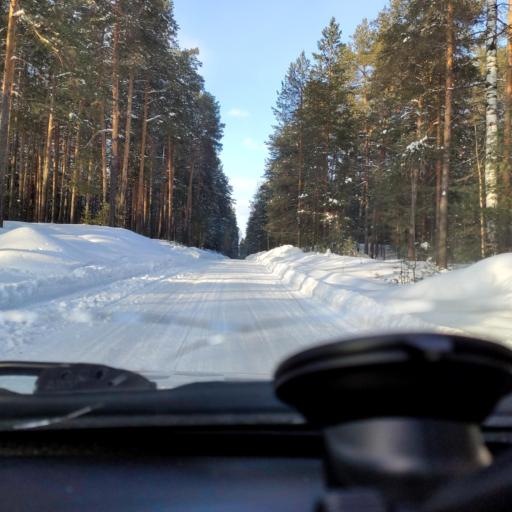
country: RU
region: Perm
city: Perm
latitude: 58.0641
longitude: 56.2608
